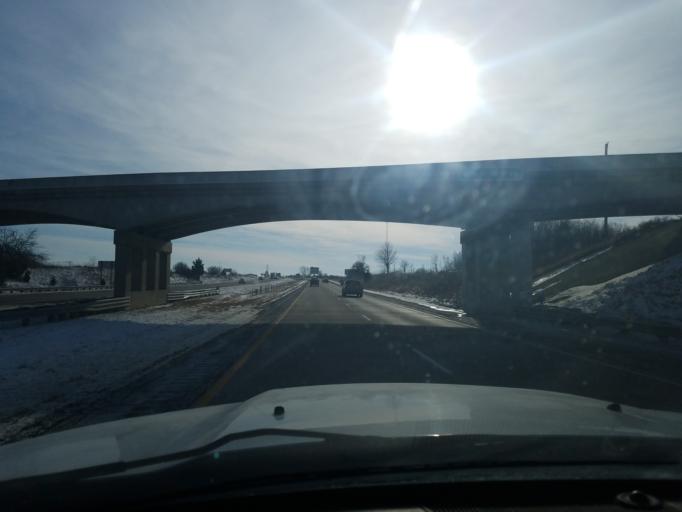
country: US
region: Indiana
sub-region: Grant County
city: Upland
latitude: 40.4343
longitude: -85.5467
